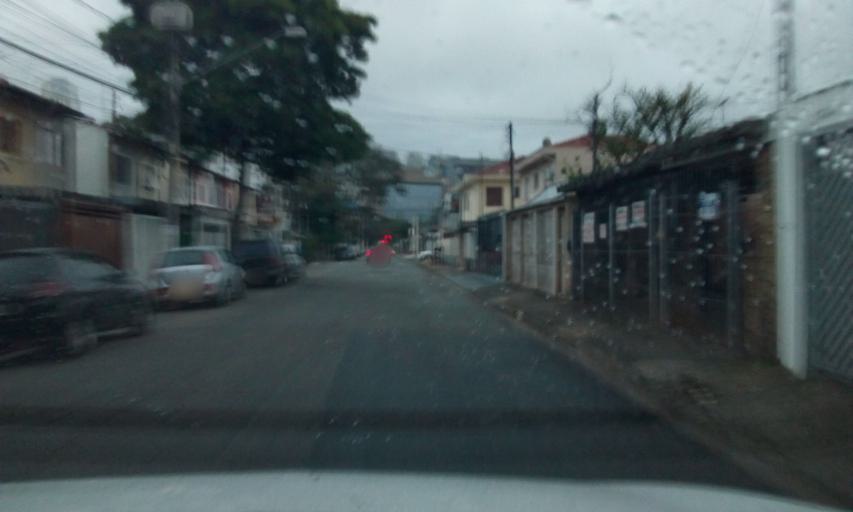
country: BR
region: Sao Paulo
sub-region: Sao Paulo
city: Sao Paulo
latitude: -23.6060
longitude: -46.6887
